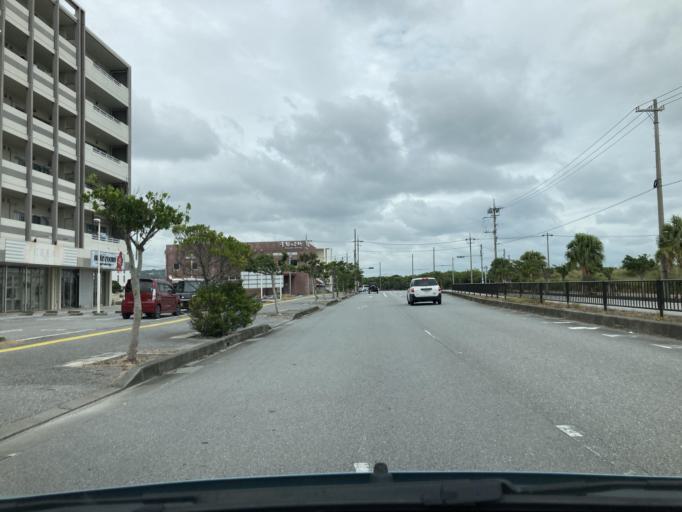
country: JP
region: Okinawa
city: Ginowan
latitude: 26.2083
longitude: 127.7636
